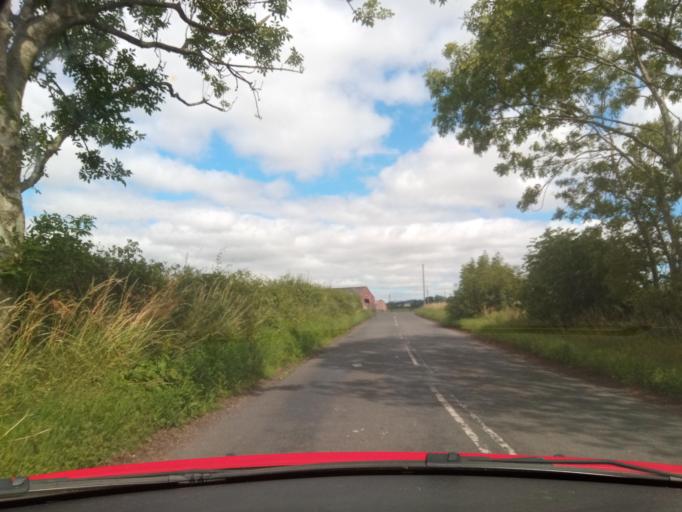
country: GB
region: Scotland
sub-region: The Scottish Borders
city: Kelso
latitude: 55.5315
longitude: -2.3613
